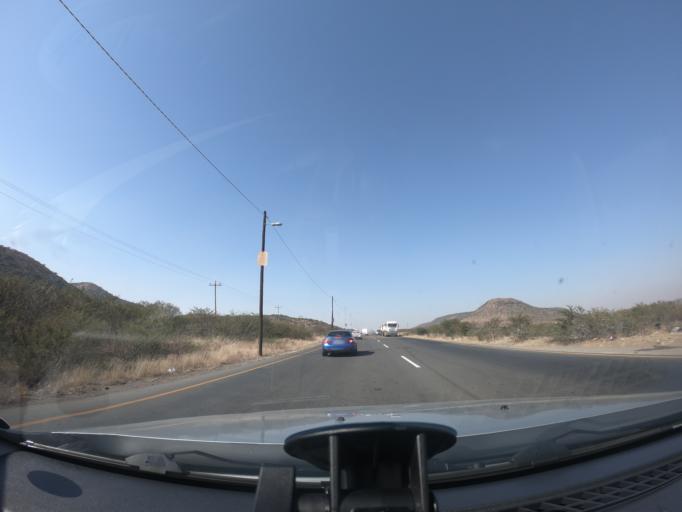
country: ZA
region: KwaZulu-Natal
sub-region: uThukela District Municipality
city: Ladysmith
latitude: -28.5566
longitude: 29.8382
